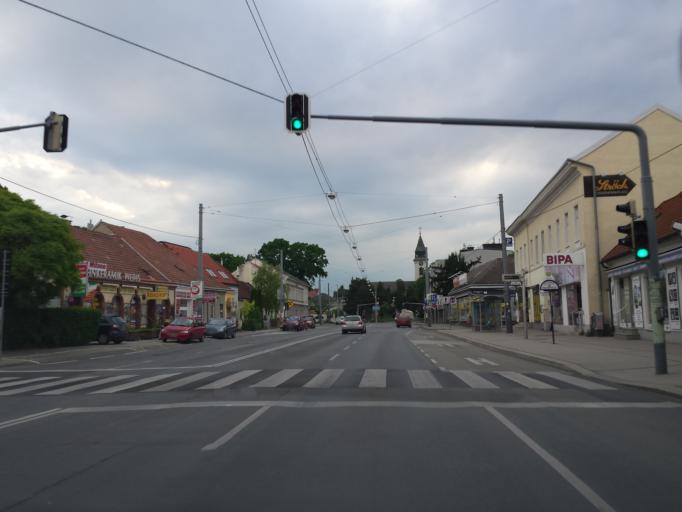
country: AT
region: Lower Austria
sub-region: Politischer Bezirk Ganserndorf
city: Gross-Enzersdorf
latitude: 48.2175
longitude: 16.4861
